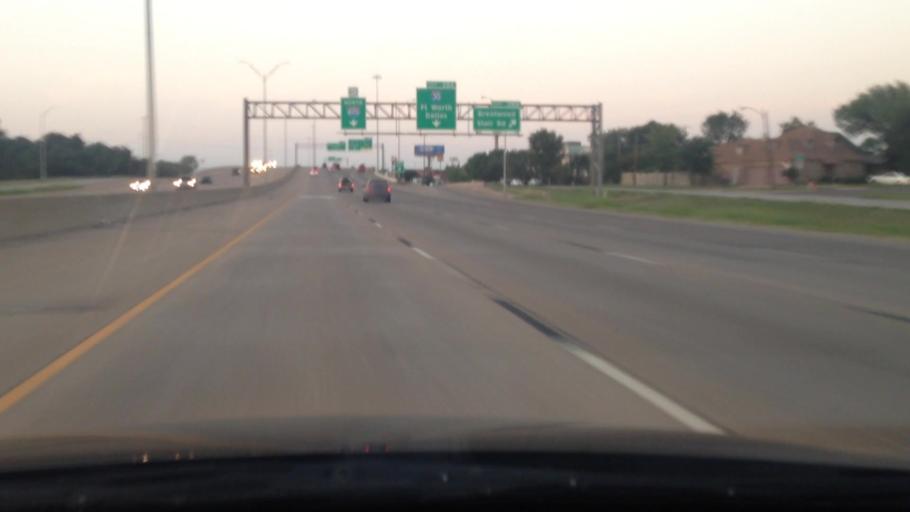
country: US
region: Texas
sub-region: Tarrant County
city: Richland Hills
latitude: 32.7500
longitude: -97.2195
